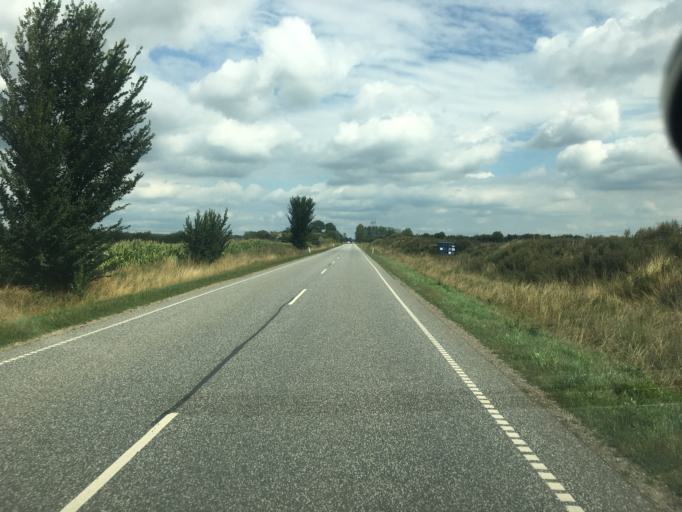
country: DK
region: South Denmark
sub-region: Aabenraa Kommune
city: Tinglev
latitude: 54.9721
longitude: 9.3143
